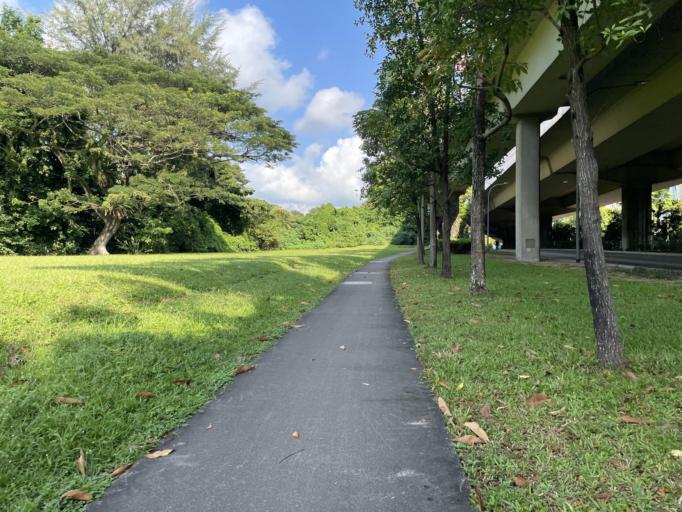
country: SG
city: Singapore
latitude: 1.2708
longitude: 103.8089
